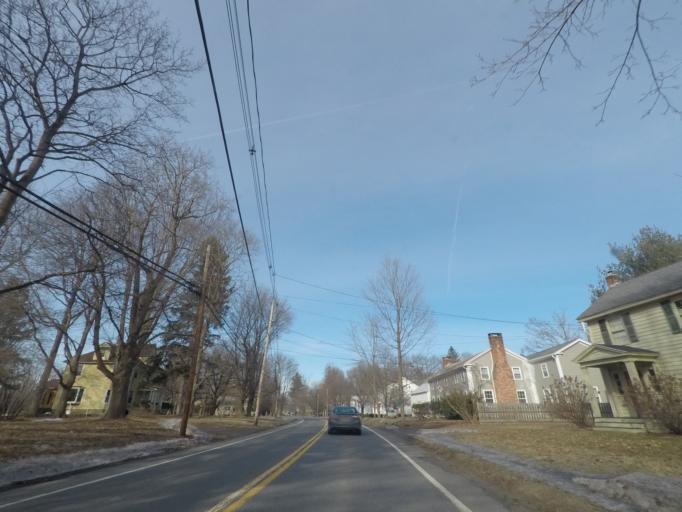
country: US
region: New York
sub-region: Columbia County
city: Niverville
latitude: 42.4694
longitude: -73.6316
